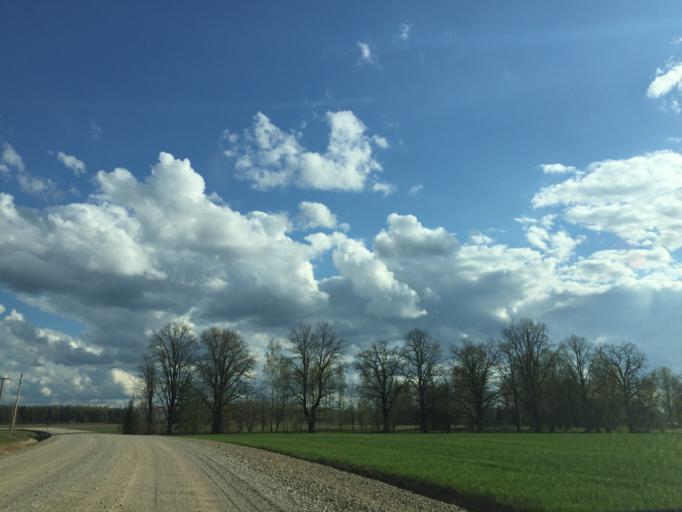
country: LV
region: Beverina
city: Murmuiza
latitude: 57.4042
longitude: 25.5095
